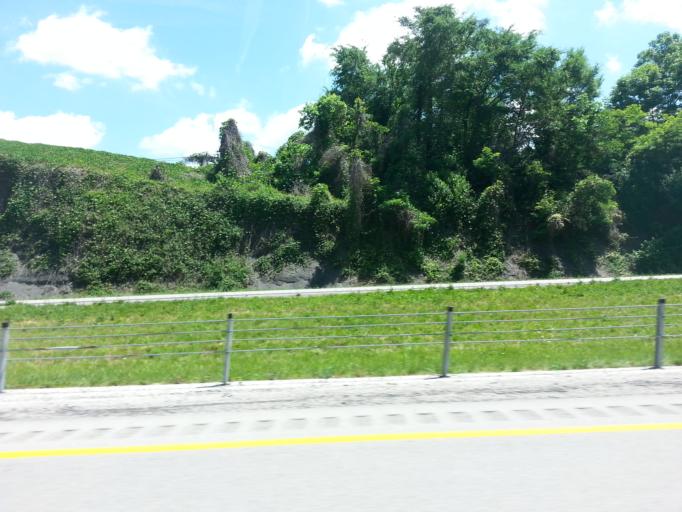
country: US
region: Kentucky
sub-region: Whitley County
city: Williamsburg
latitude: 36.7450
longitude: -84.1763
